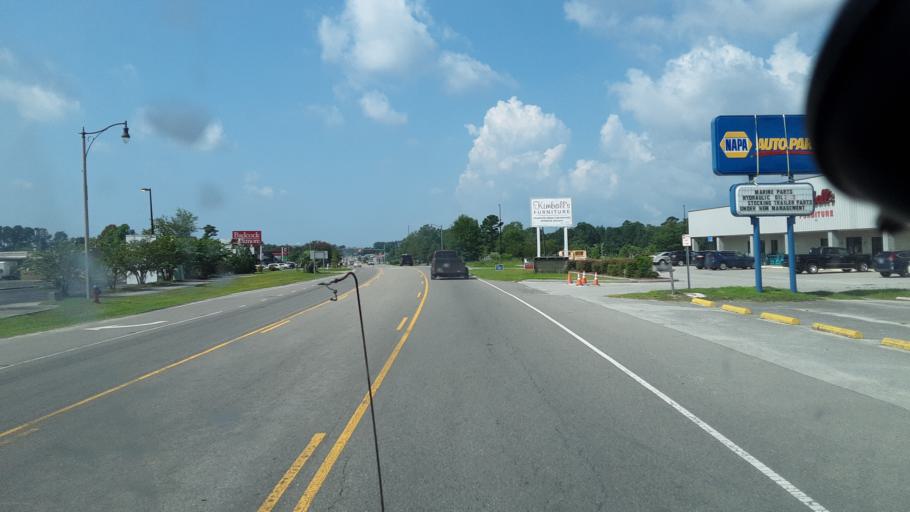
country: US
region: North Carolina
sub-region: Brunswick County
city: Shallotte
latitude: 33.9834
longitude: -78.3706
